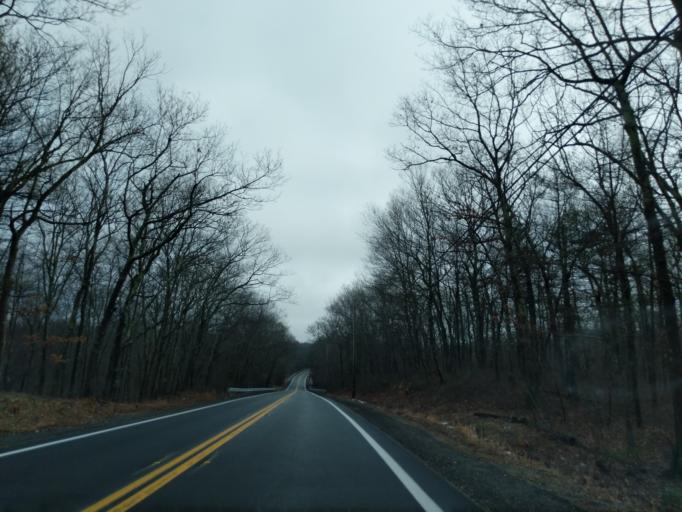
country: US
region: Massachusetts
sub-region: Worcester County
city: Douglas
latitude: 42.0565
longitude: -71.7941
